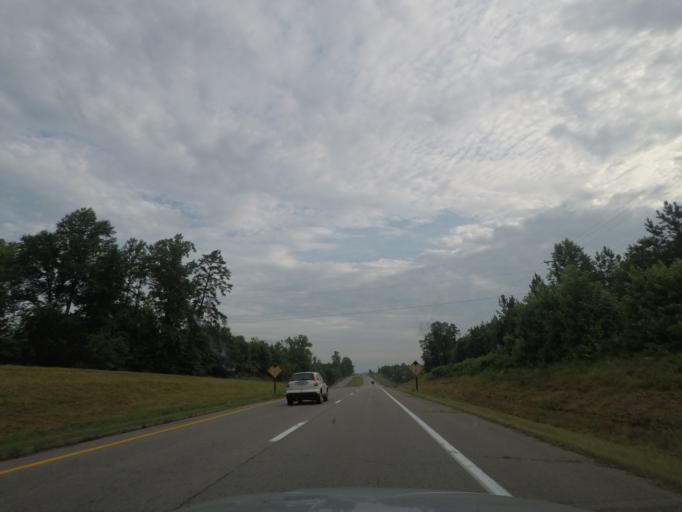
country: US
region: Virginia
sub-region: Halifax County
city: South Boston
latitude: 36.6753
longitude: -78.8972
